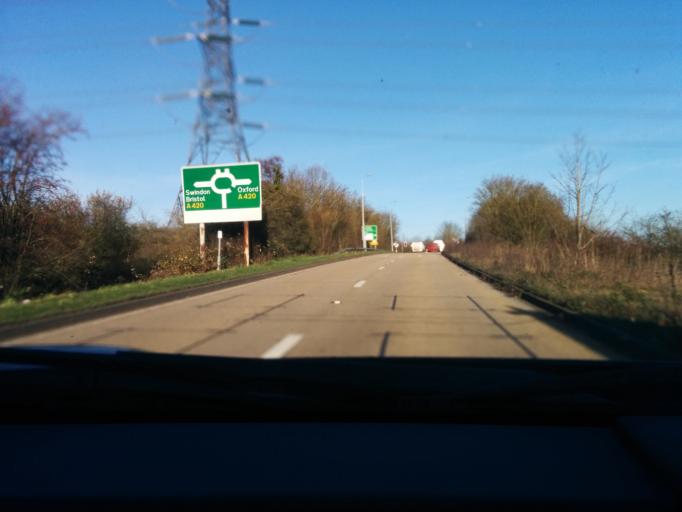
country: GB
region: England
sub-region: Oxfordshire
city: Boars Hill
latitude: 51.7543
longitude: -1.2971
